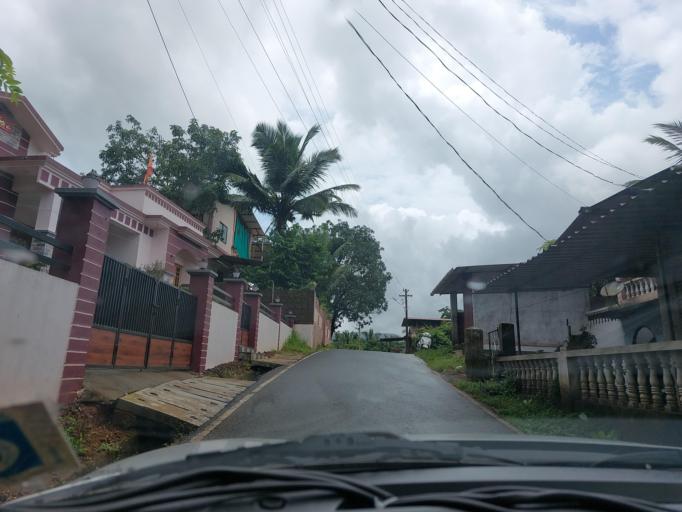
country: IN
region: Goa
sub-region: North Goa
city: Valpoy
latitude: 15.5385
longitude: 74.1411
